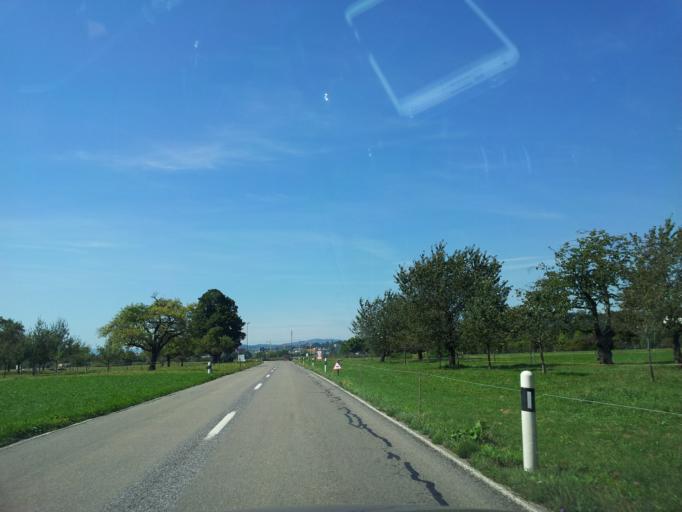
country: CH
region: Saint Gallen
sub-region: Wahlkreis See-Gaster
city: Jona
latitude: 47.2208
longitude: 8.8689
